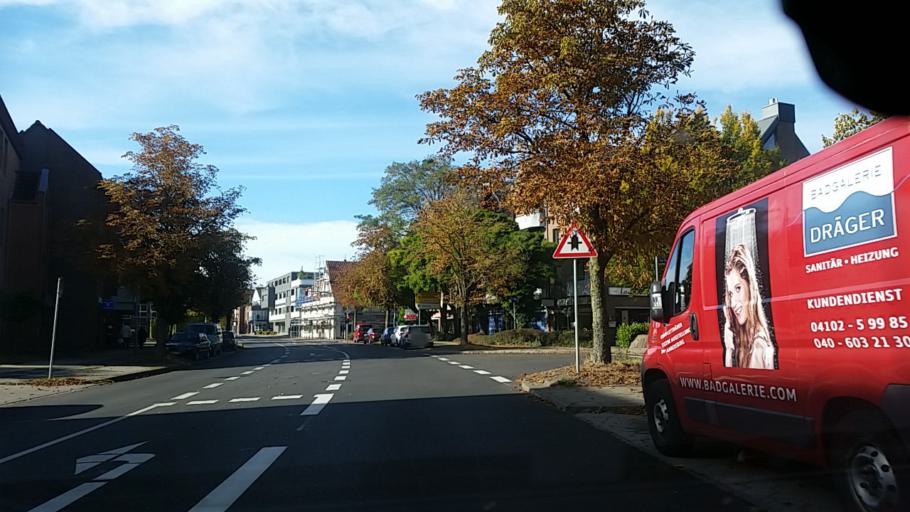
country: DE
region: Schleswig-Holstein
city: Ahrensburg
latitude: 53.6754
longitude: 10.2414
